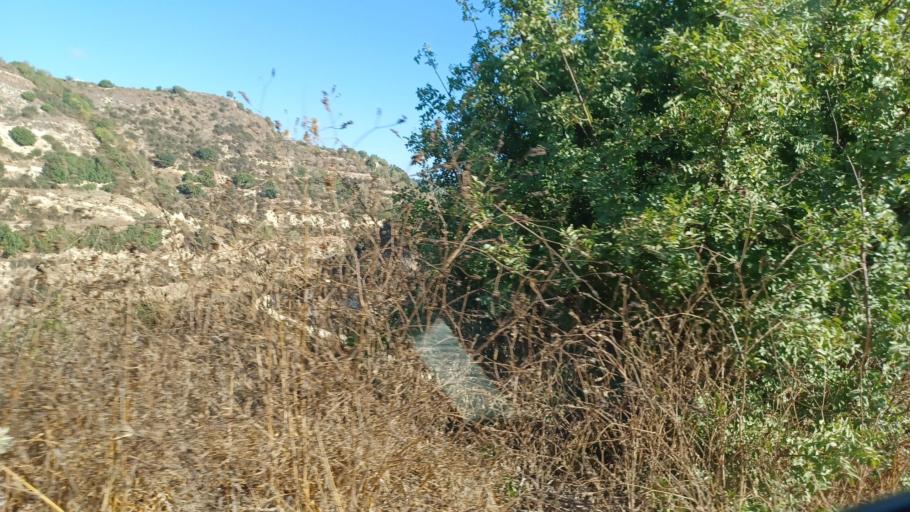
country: CY
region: Pafos
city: Mesogi
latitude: 34.8424
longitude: 32.5191
